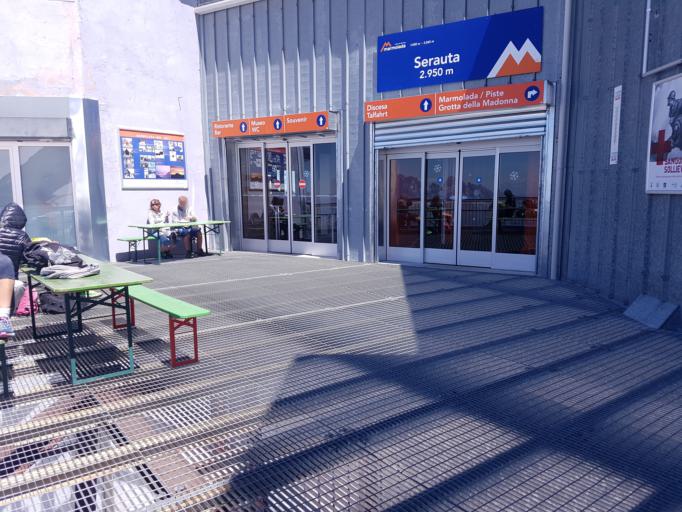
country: IT
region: Veneto
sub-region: Provincia di Belluno
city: Pie' Falcade
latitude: 46.4375
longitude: 11.8791
